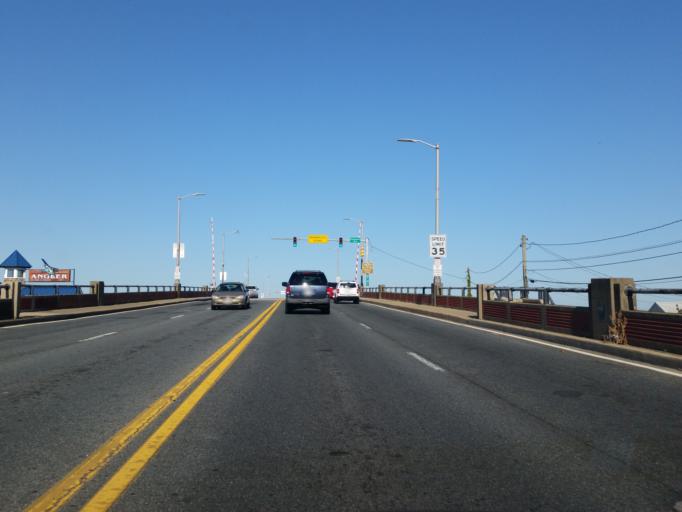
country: US
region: Maryland
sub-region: Worcester County
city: Ocean City
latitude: 38.3318
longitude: -75.0885
